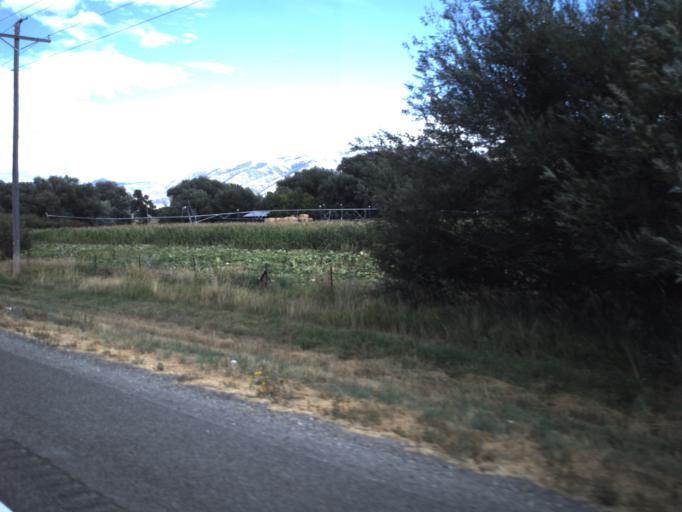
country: US
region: Utah
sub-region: Cache County
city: Wellsville
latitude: 41.6397
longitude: -111.9175
